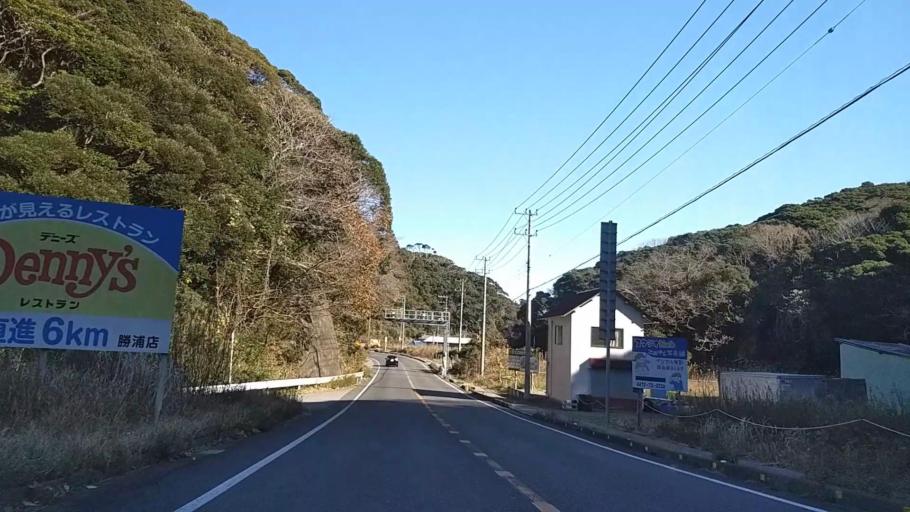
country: JP
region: Chiba
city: Katsuura
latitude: 35.1432
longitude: 140.2853
